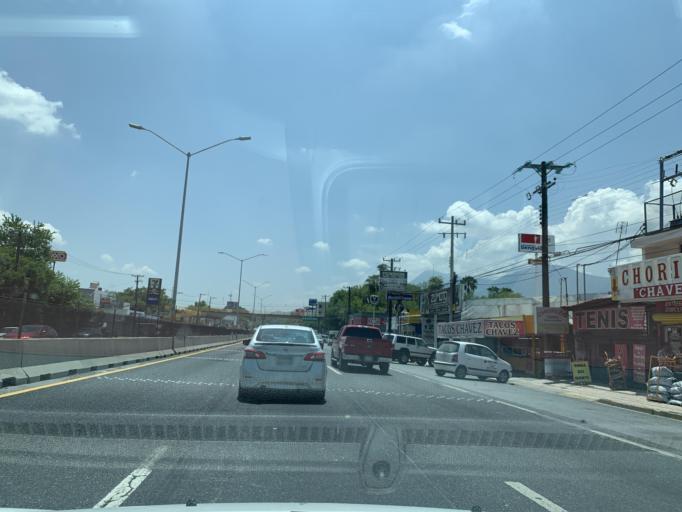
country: MX
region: Nuevo Leon
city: Santiago
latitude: 25.4060
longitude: -100.1344
